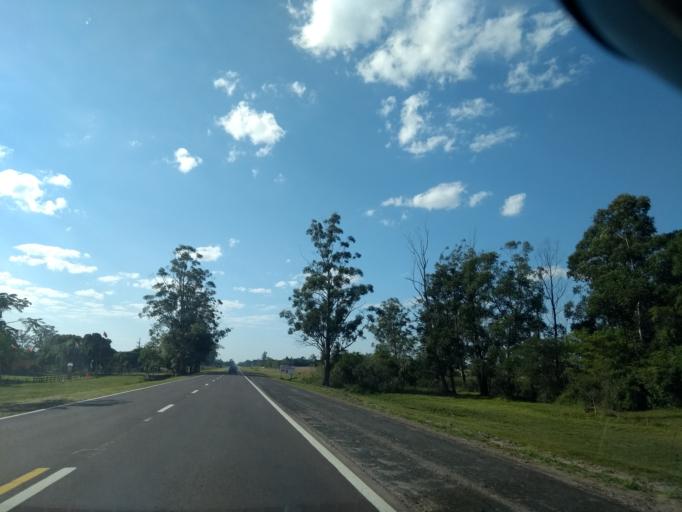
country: AR
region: Corrientes
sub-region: Departamento de San Cosme
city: San Cosme
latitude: -27.3672
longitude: -58.3631
